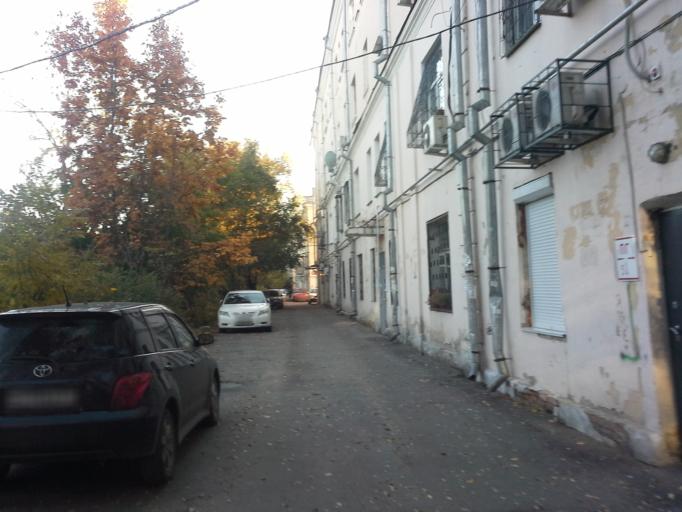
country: RU
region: Khabarovsk Krai
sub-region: Khabarovskiy Rayon
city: Khabarovsk
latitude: 48.4869
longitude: 135.0627
